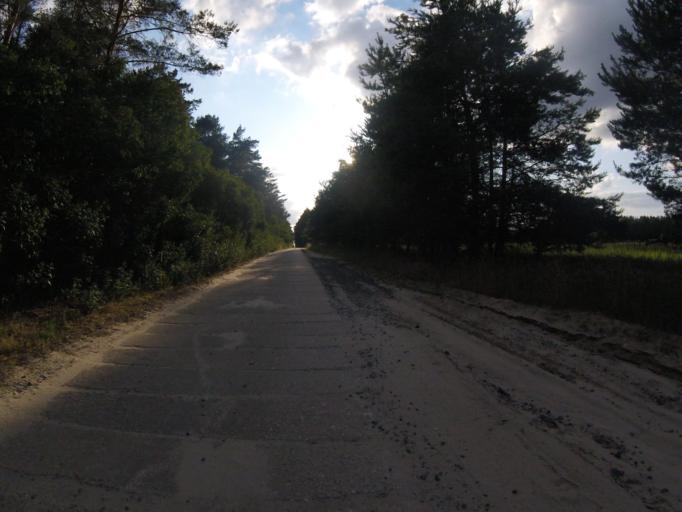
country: DE
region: Brandenburg
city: Schwerin
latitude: 52.1968
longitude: 13.6089
